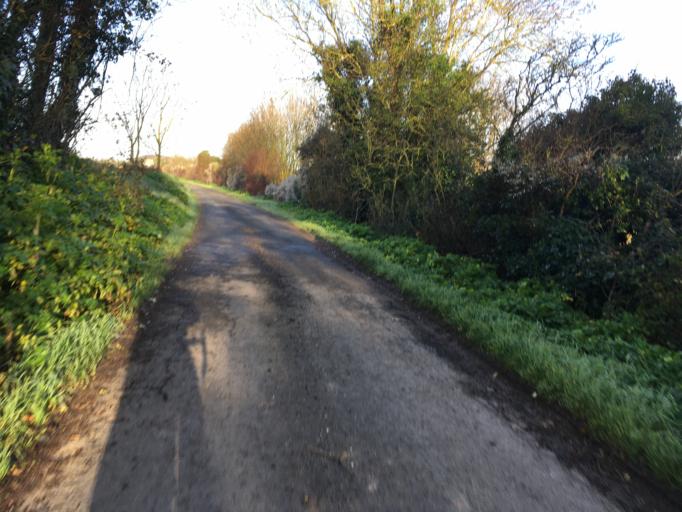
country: FR
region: Poitou-Charentes
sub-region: Departement de la Charente-Maritime
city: Nieul-sur-Mer
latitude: 46.1970
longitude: -1.1763
